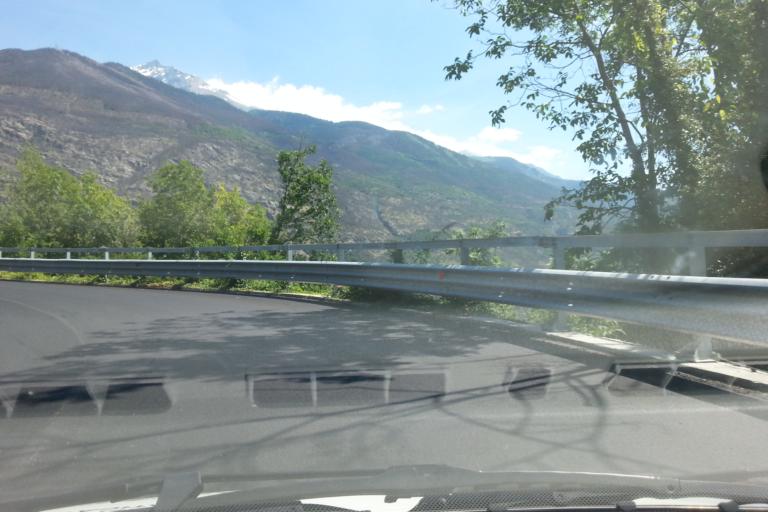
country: IT
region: Piedmont
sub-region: Provincia di Torino
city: Giaglione
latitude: 45.1448
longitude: 7.0184
